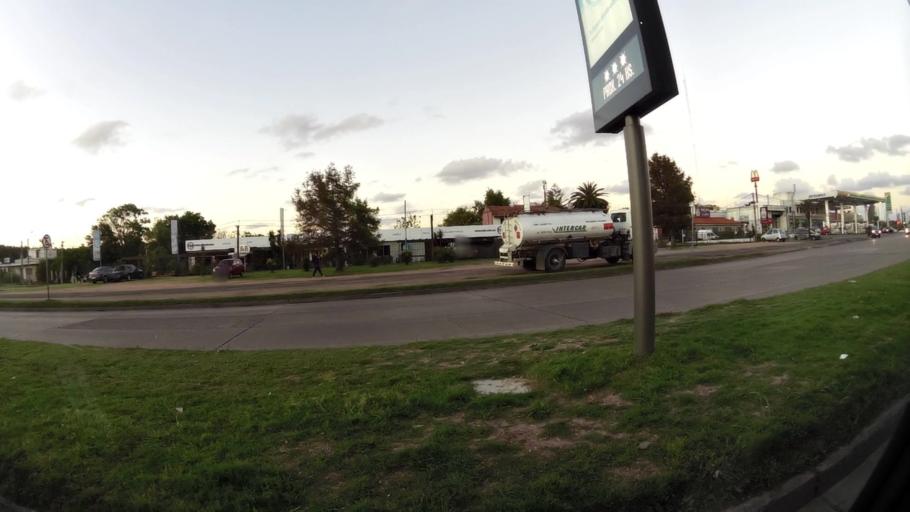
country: UY
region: Canelones
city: Paso de Carrasco
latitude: -34.8833
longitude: -56.0847
